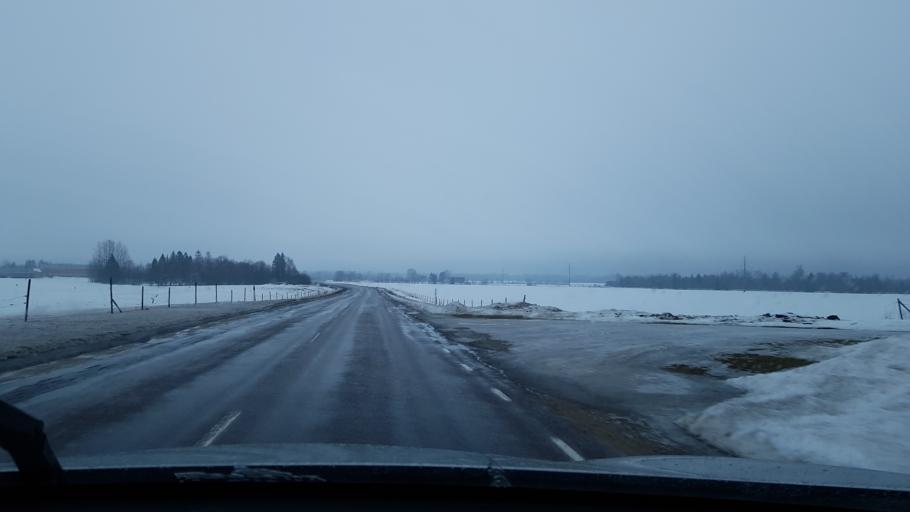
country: EE
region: Harju
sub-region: Nissi vald
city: Turba
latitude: 58.9086
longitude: 24.1347
